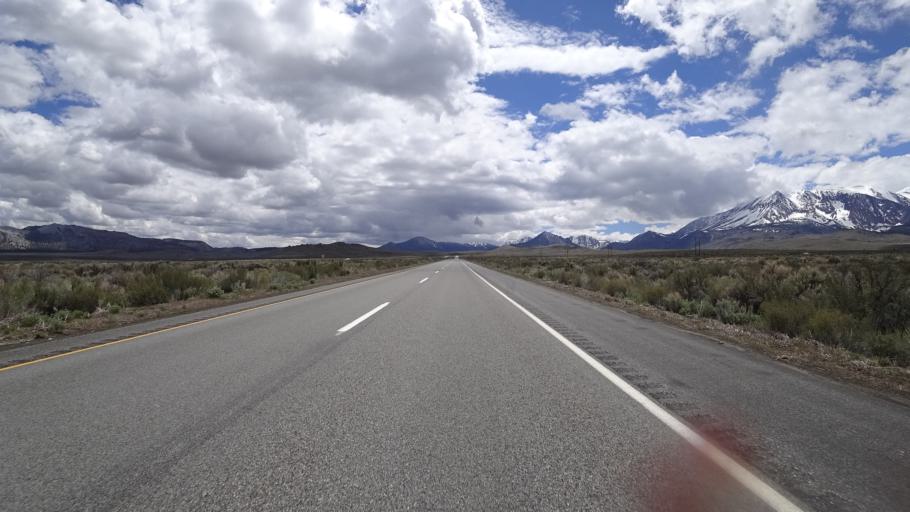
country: US
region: California
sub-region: Mono County
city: Mammoth Lakes
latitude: 37.8835
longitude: -119.0907
